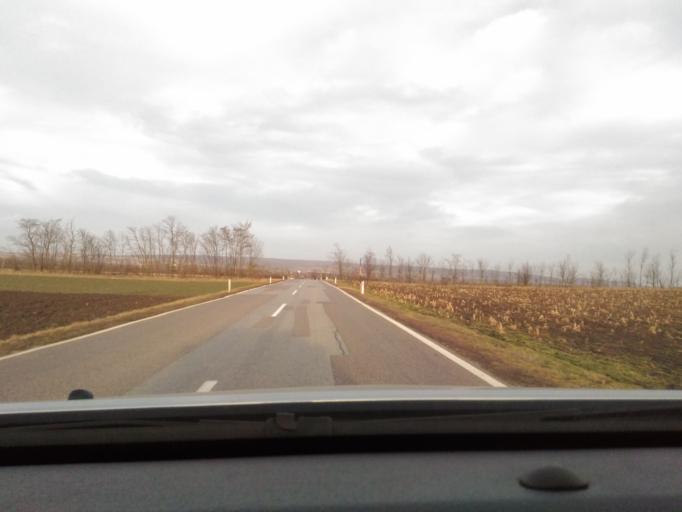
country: AT
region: Lower Austria
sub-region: Politischer Bezirk Mistelbach
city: Neudorf bei Staatz
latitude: 48.7176
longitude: 16.4576
